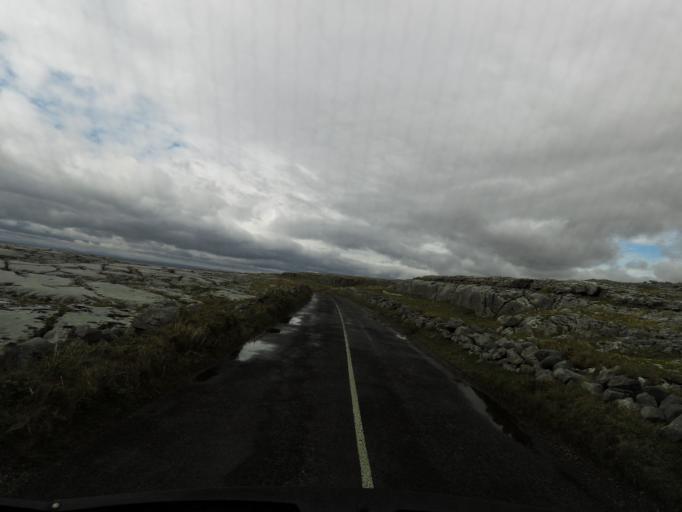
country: IE
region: Connaught
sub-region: County Galway
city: Bearna
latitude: 53.0615
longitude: -9.3619
